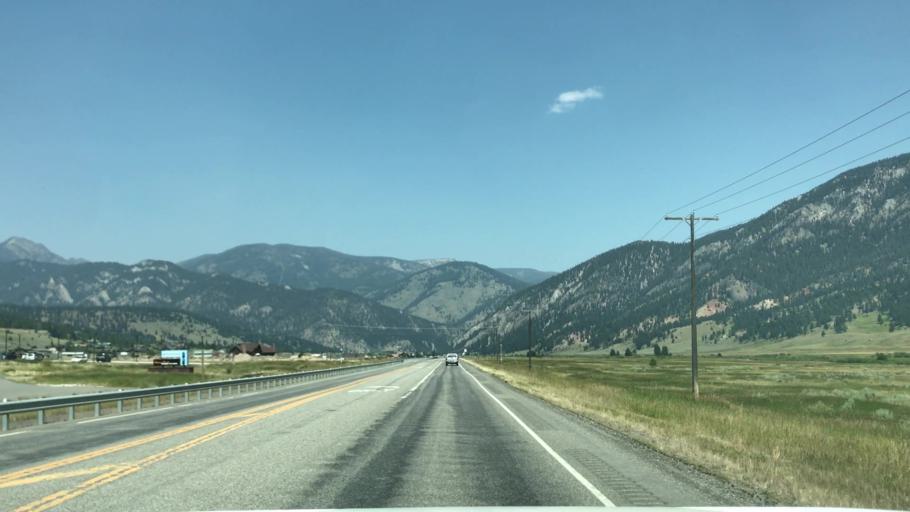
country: US
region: Montana
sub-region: Gallatin County
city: Big Sky
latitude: 45.2298
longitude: -111.2508
